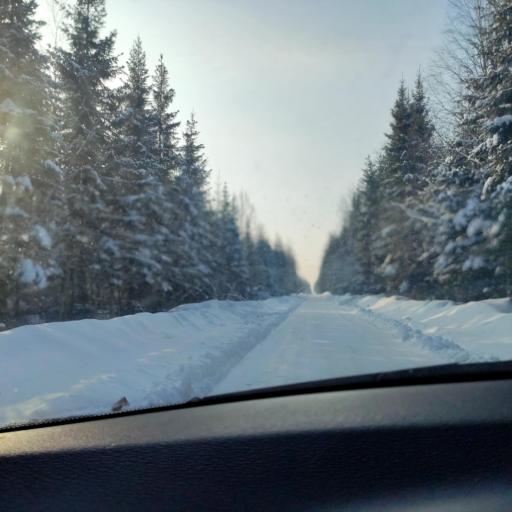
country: RU
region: Perm
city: Kondratovo
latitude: 58.0746
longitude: 56.1290
